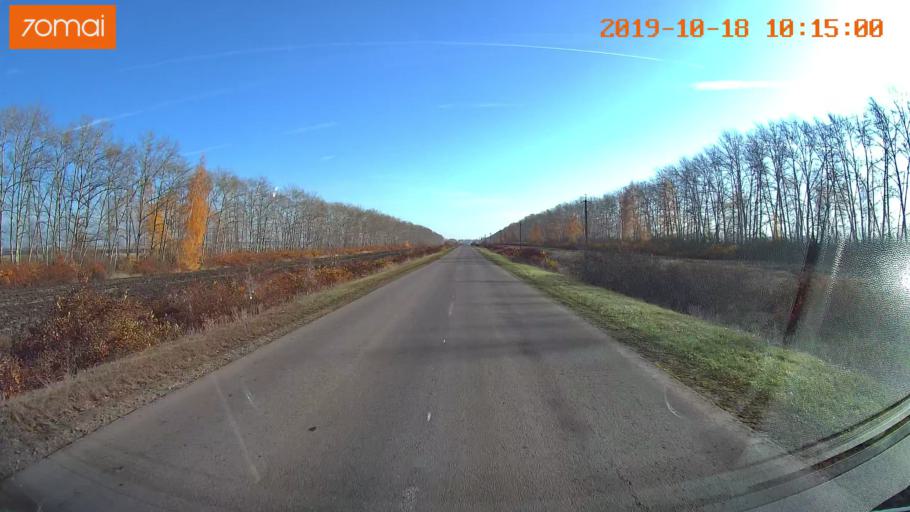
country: RU
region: Tula
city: Kurkino
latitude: 53.4069
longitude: 38.5578
